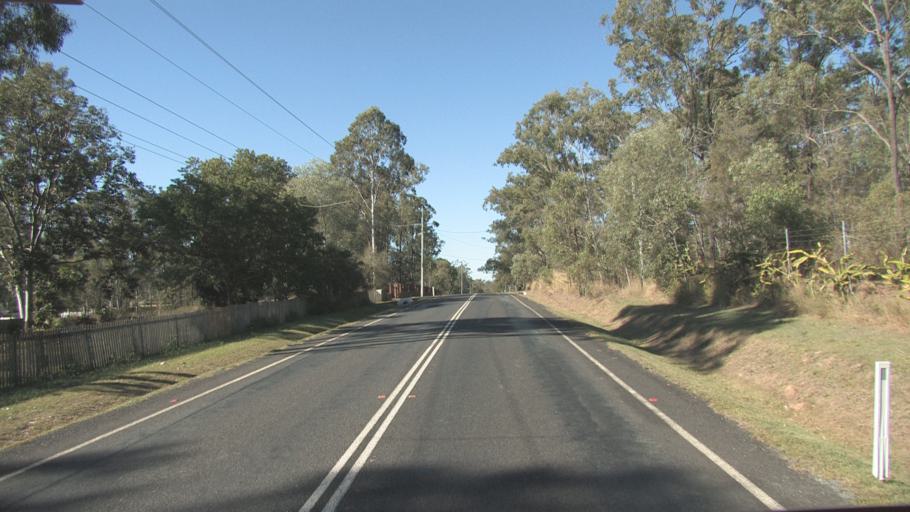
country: AU
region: Queensland
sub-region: Logan
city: Park Ridge South
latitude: -27.7240
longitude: 153.0140
